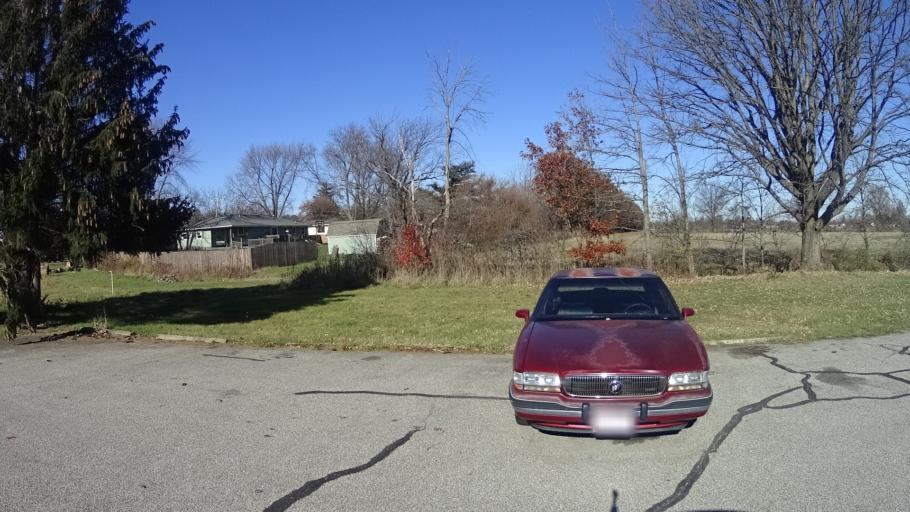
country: US
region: Ohio
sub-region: Lorain County
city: Elyria
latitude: 41.3659
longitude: -82.1587
